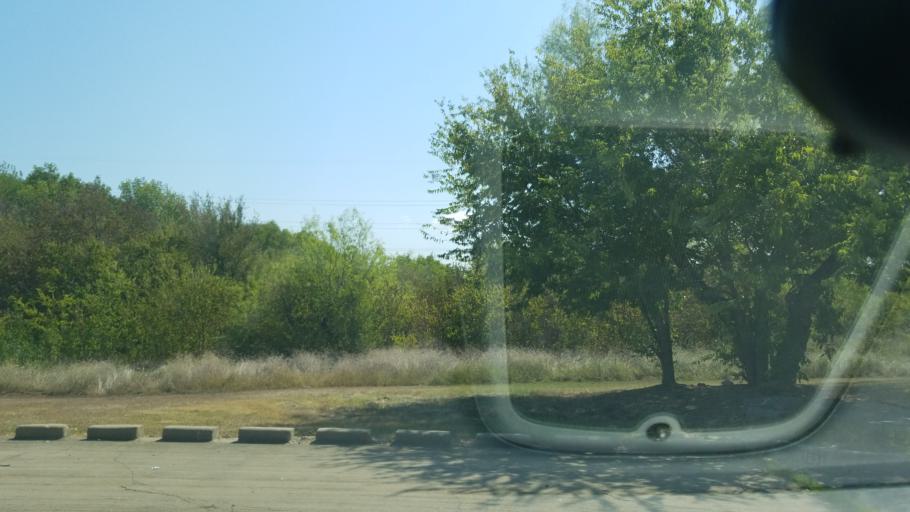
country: US
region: Texas
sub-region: Dallas County
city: Grand Prairie
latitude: 32.7063
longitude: -96.9802
